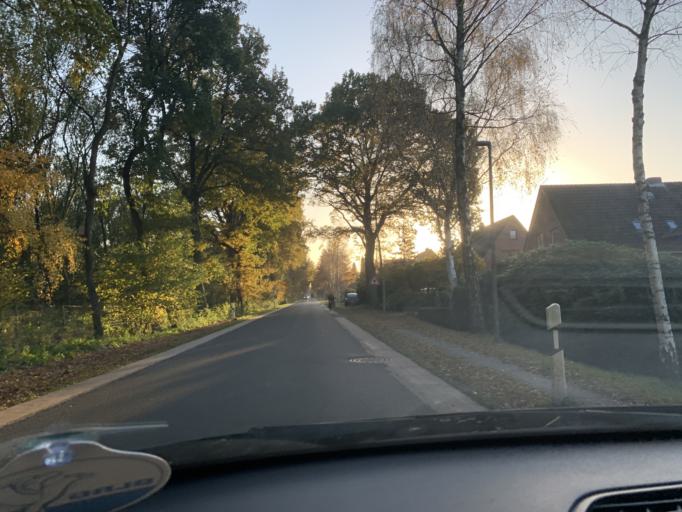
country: DE
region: Lower Saxony
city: Bad Zwischenahn
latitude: 53.1666
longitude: 8.0659
